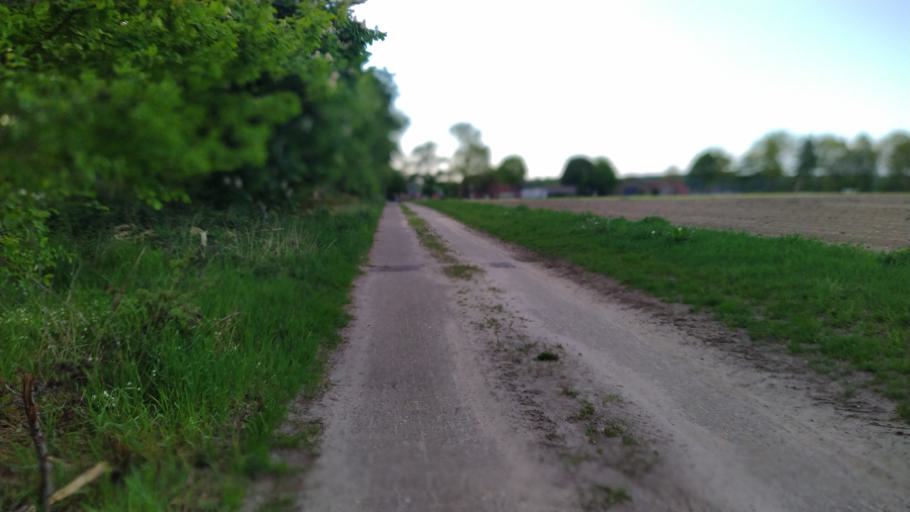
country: DE
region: Lower Saxony
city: Farven
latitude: 53.4351
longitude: 9.3283
